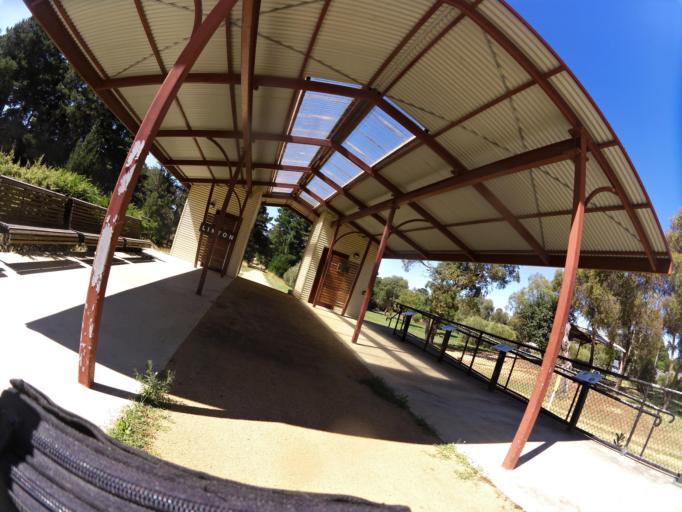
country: AU
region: Victoria
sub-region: Ballarat North
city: Delacombe
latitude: -37.6831
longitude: 143.5661
